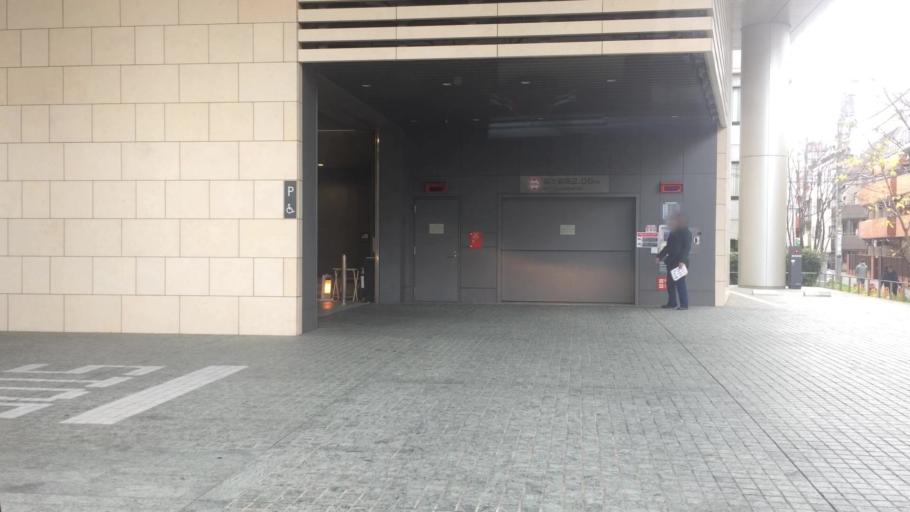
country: JP
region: Tokyo
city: Tokyo
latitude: 35.6482
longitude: 139.7150
